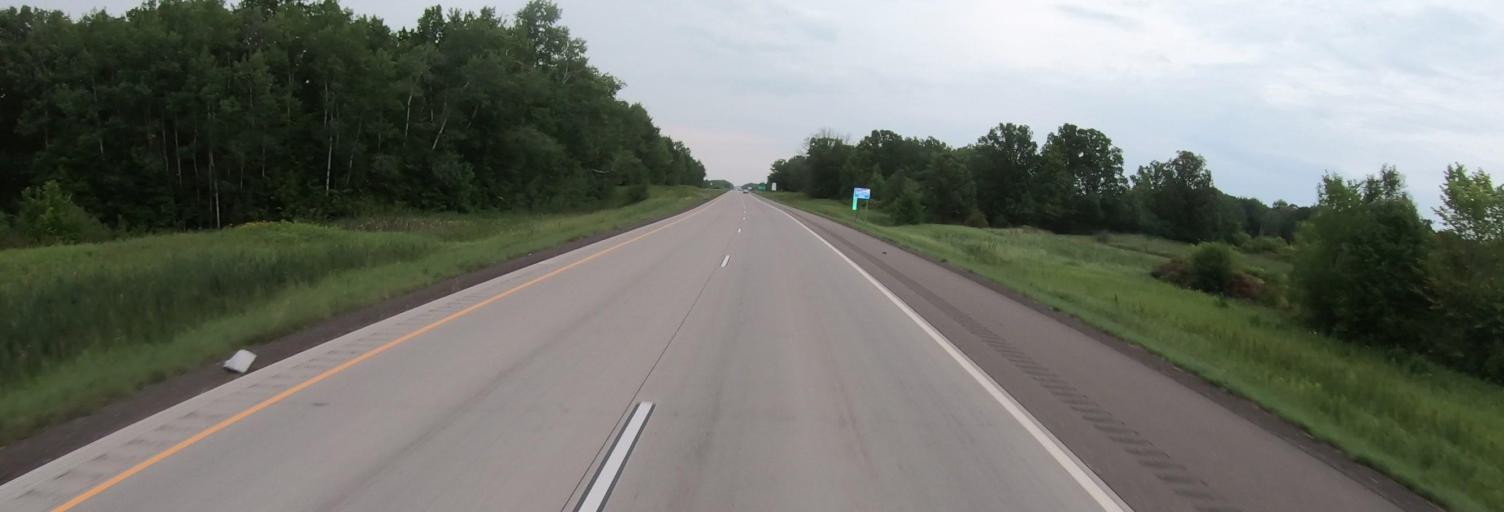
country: US
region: Minnesota
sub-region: Pine County
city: Pine City
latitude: 45.8558
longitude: -92.9719
